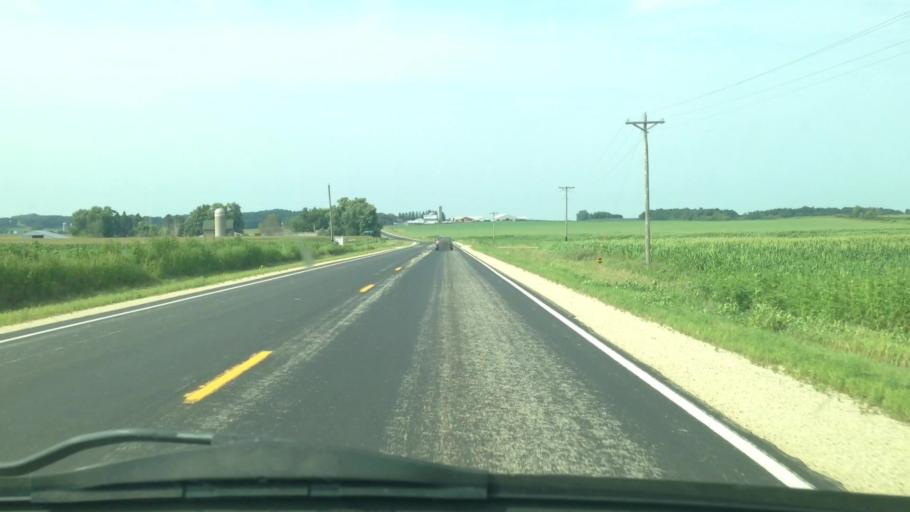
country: US
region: Minnesota
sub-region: Winona County
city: Lewiston
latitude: 43.9467
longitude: -91.9547
